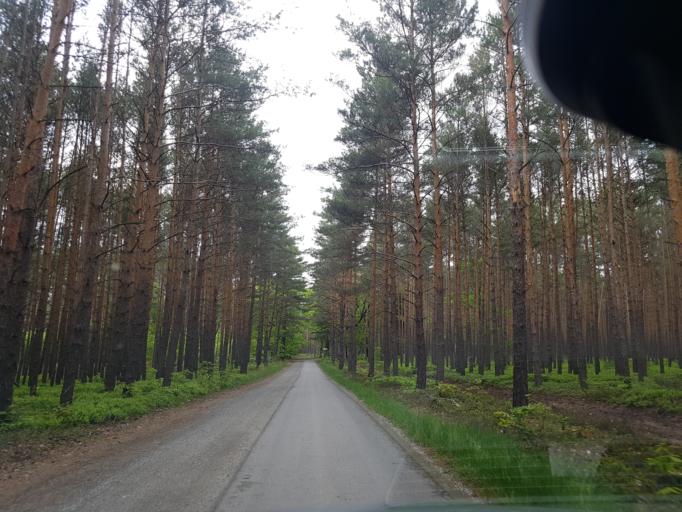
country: DE
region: Brandenburg
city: Crinitz
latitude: 51.6977
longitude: 13.7745
